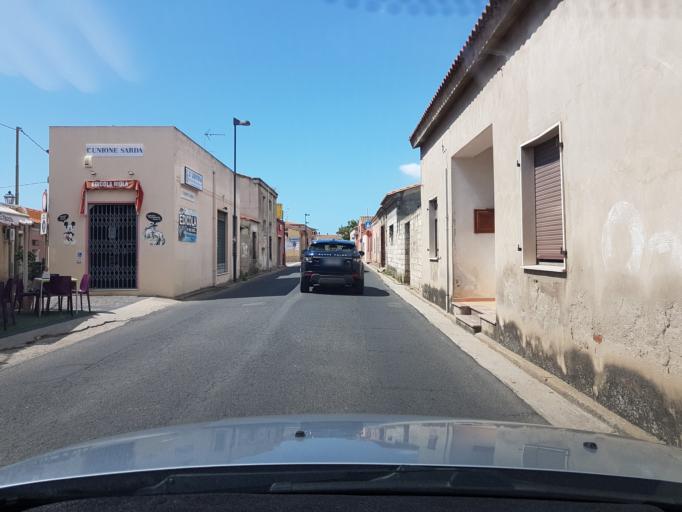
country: IT
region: Sardinia
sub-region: Provincia di Oristano
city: Riola Sardo
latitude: 39.9943
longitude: 8.5408
